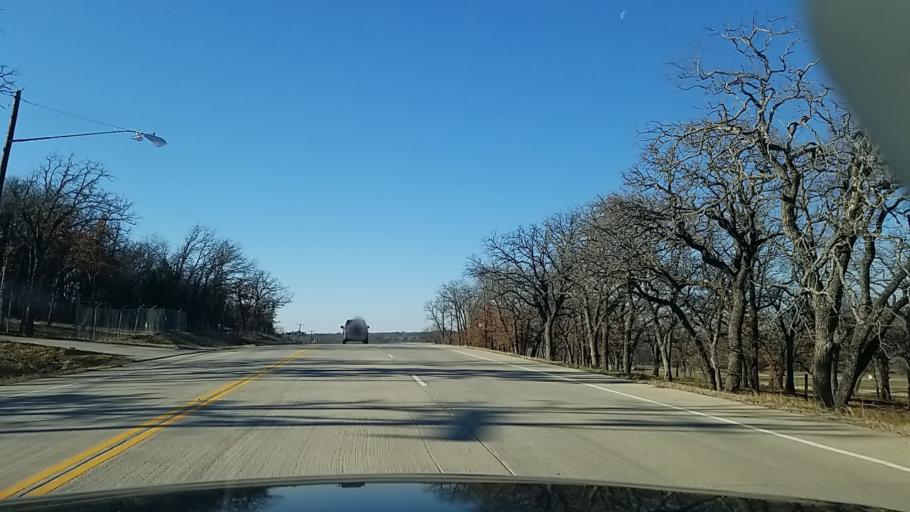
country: US
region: Texas
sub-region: Denton County
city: Argyle
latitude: 33.1297
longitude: -97.1772
